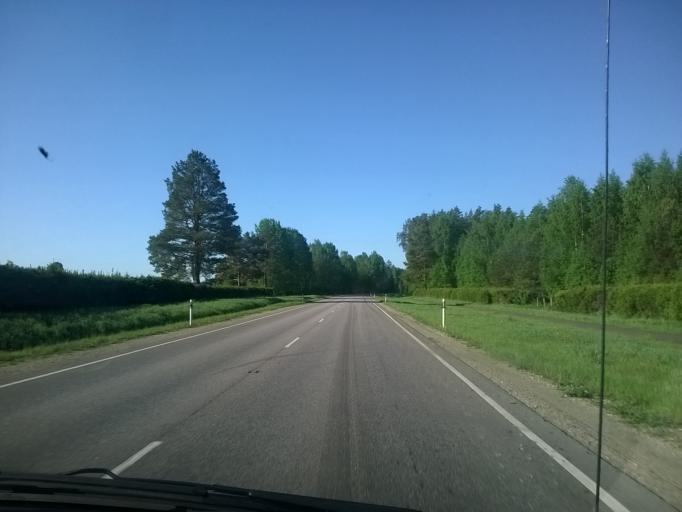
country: EE
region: Valgamaa
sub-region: Valga linn
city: Valga
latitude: 57.8363
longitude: 26.1248
